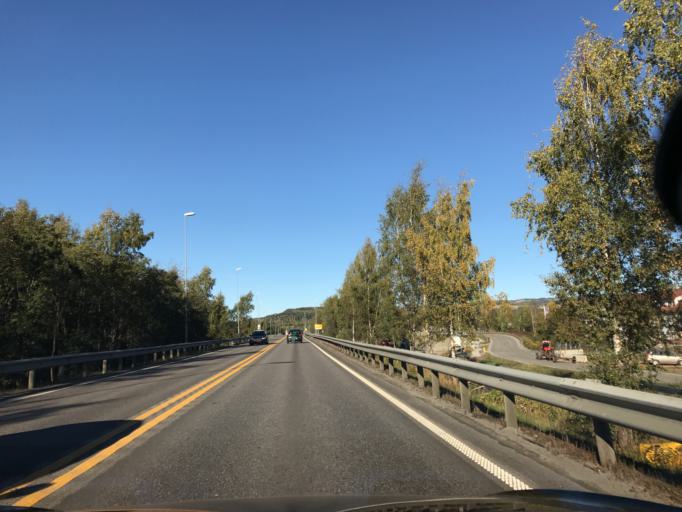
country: NO
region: Hedmark
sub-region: Ringsaker
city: Brumunddal
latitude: 60.8770
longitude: 10.9344
